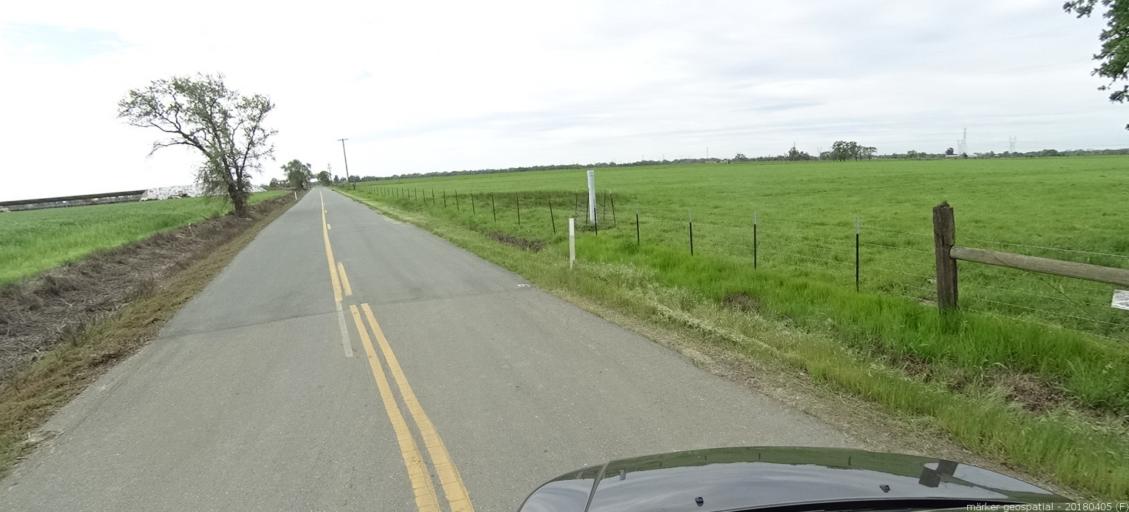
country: US
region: California
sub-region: Sacramento County
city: Galt
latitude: 38.2544
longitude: -121.3556
